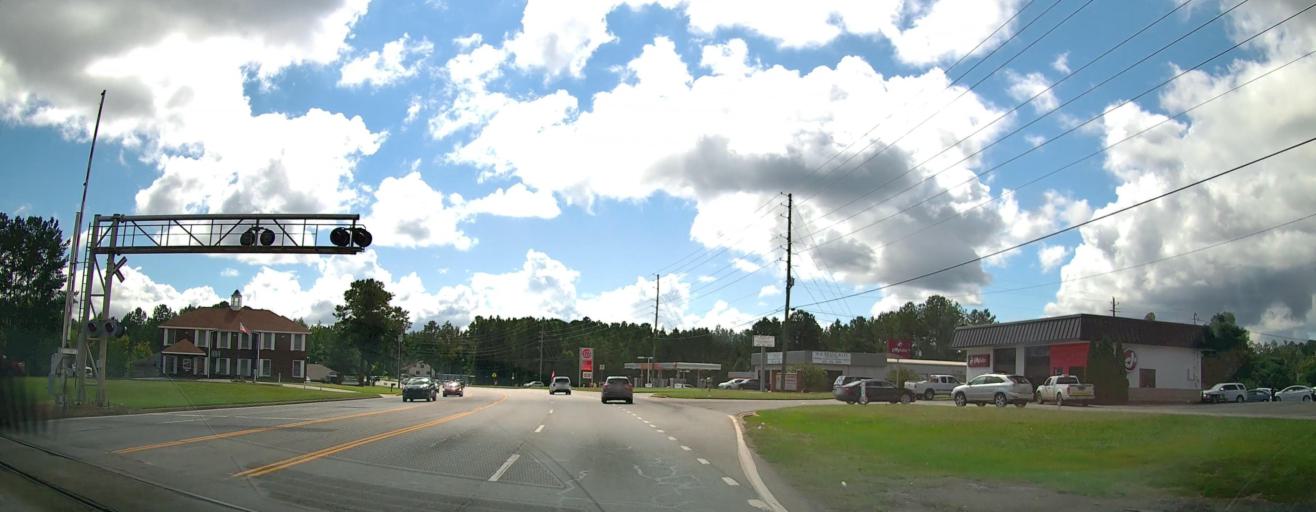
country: US
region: Georgia
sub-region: Baldwin County
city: Milledgeville
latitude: 33.1047
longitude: -83.2601
